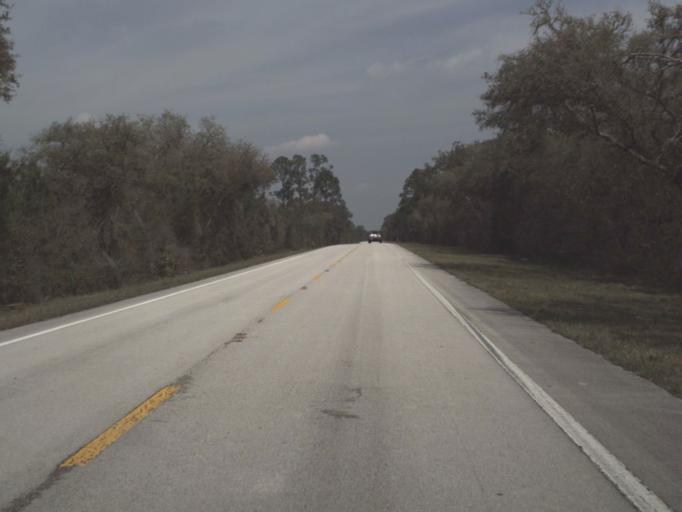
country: US
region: Florida
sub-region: Lake County
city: Astor
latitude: 29.1924
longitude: -81.6560
